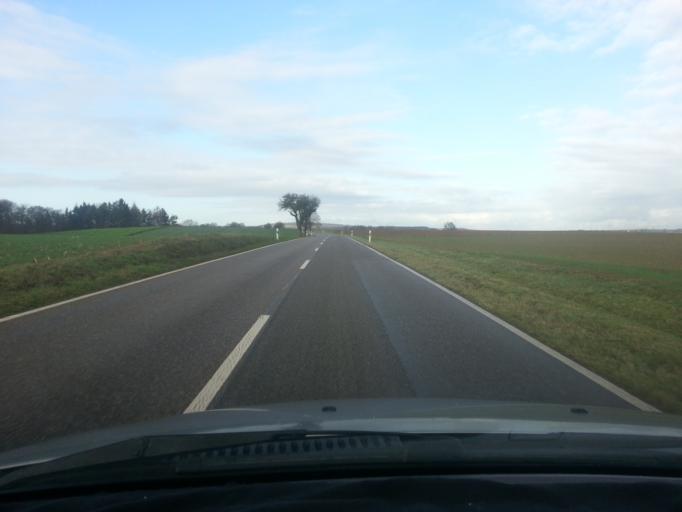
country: DE
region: Baden-Wuerttemberg
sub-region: Regierungsbezirk Stuttgart
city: Eppingen
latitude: 49.1609
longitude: 8.8633
